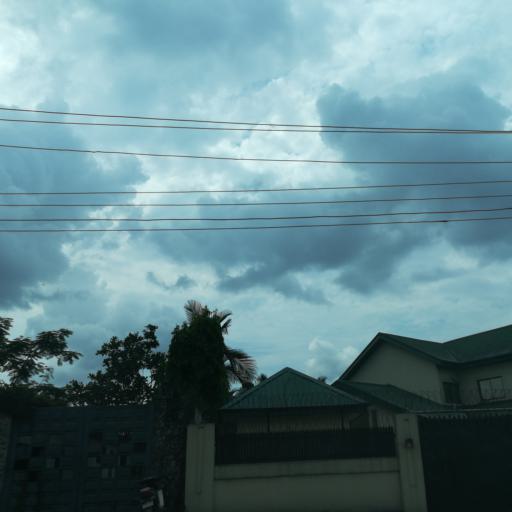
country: NG
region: Rivers
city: Port Harcourt
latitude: 4.8264
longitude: 7.0007
